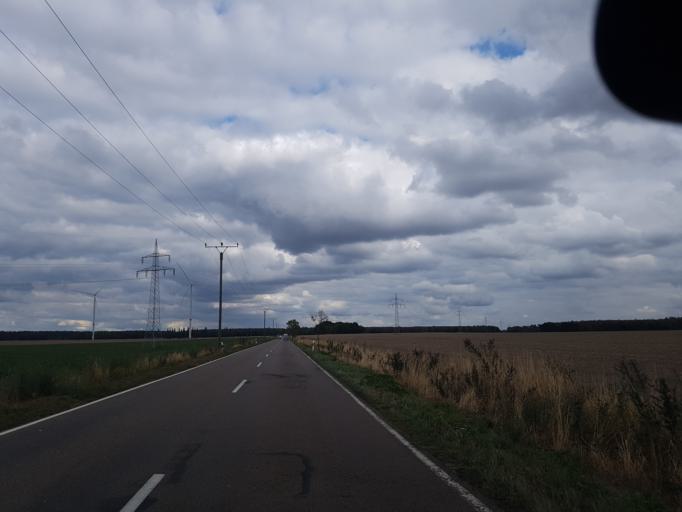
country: DE
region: Saxony-Anhalt
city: Klieken
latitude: 51.9278
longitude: 12.3314
